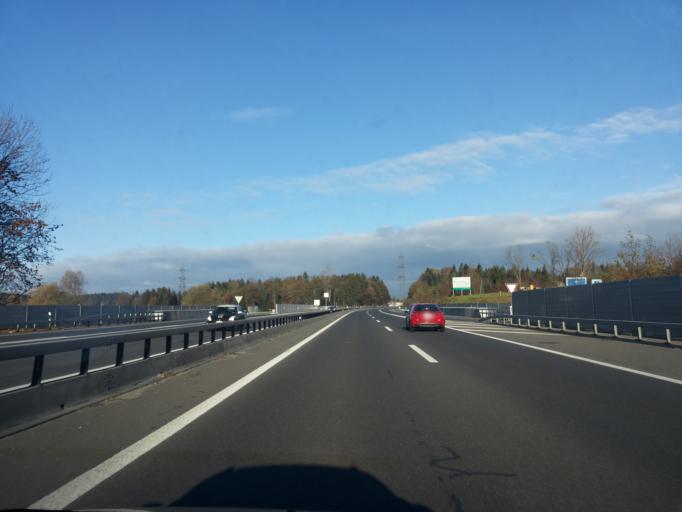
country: CH
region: Lucerne
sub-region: Hochdorf District
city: Emmen
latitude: 47.0886
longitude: 8.2521
